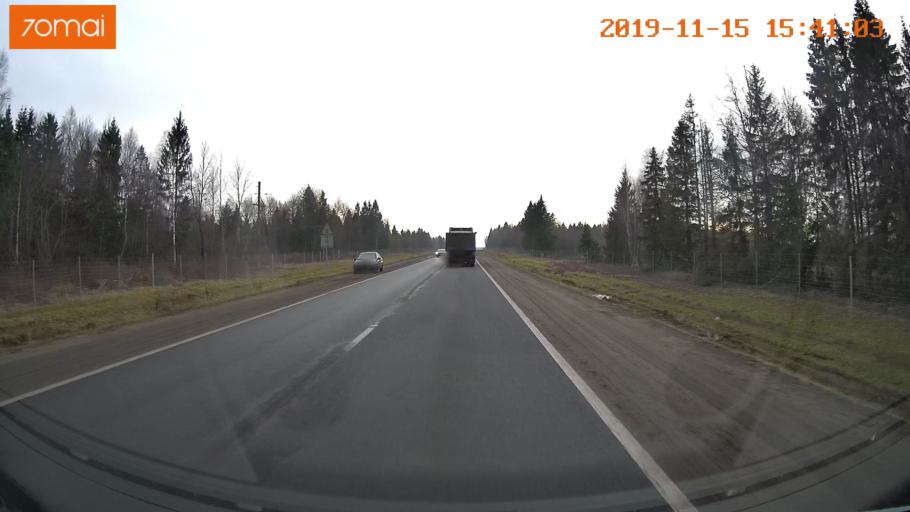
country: RU
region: Jaroslavl
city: Danilov
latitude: 58.0049
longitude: 40.0513
